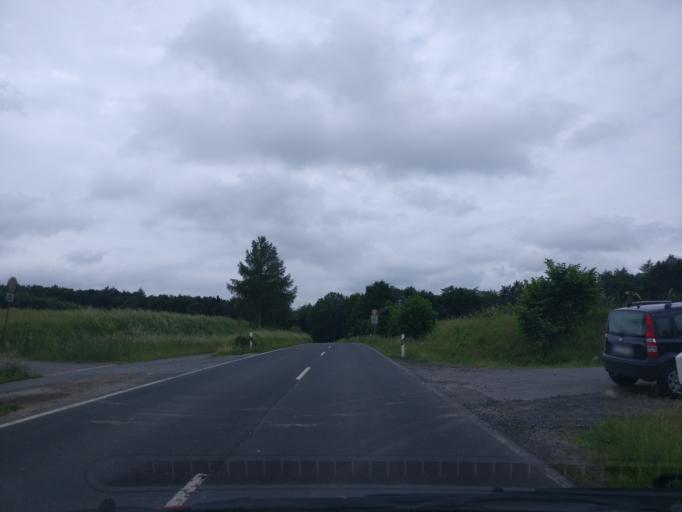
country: DE
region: Lower Saxony
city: Scheden
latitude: 51.4225
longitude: 9.7019
